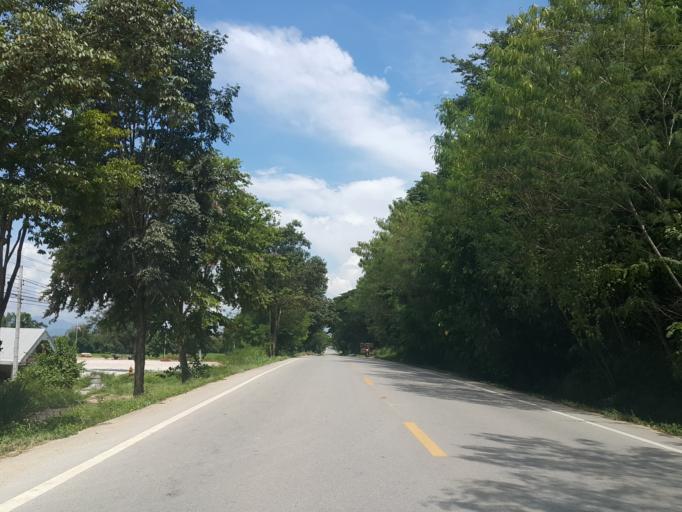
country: TH
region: Chiang Mai
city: Phrao
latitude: 19.2866
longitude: 99.1876
